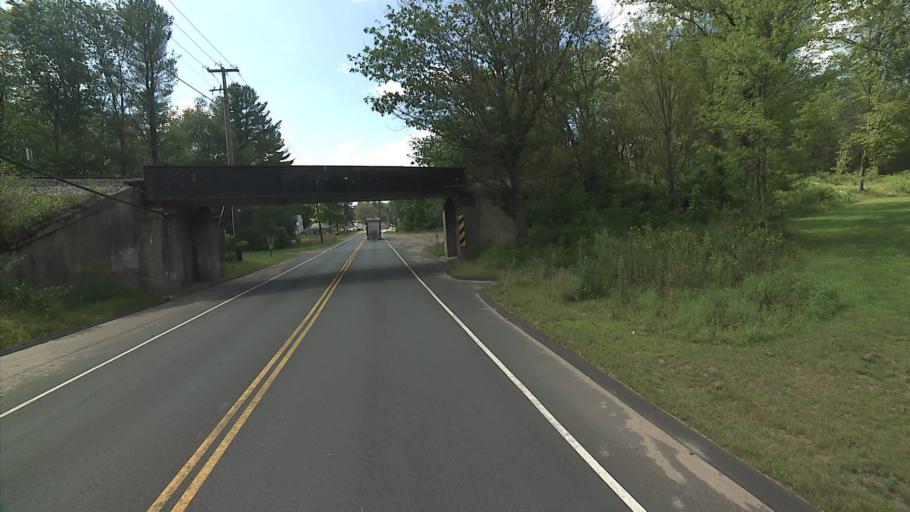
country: US
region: Connecticut
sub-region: Tolland County
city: Stafford Springs
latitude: 41.9650
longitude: -72.3236
